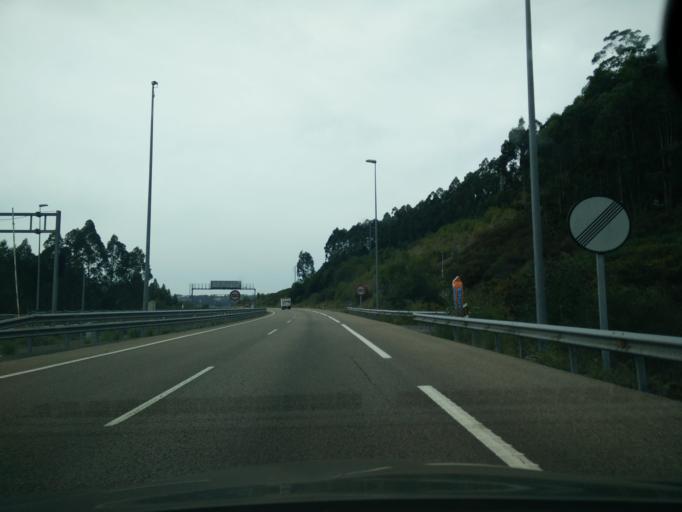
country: ES
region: Asturias
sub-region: Province of Asturias
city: Arriba
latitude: 43.4939
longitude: -5.5323
